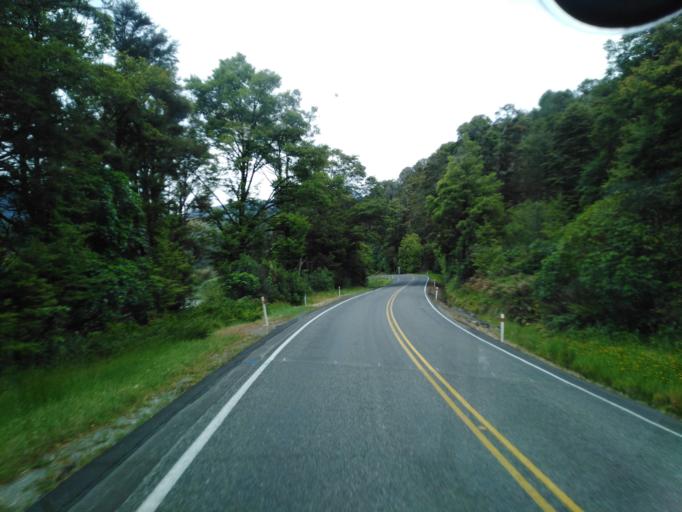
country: NZ
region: Tasman
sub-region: Tasman District
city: Wakefield
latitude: -41.7073
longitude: 172.5839
